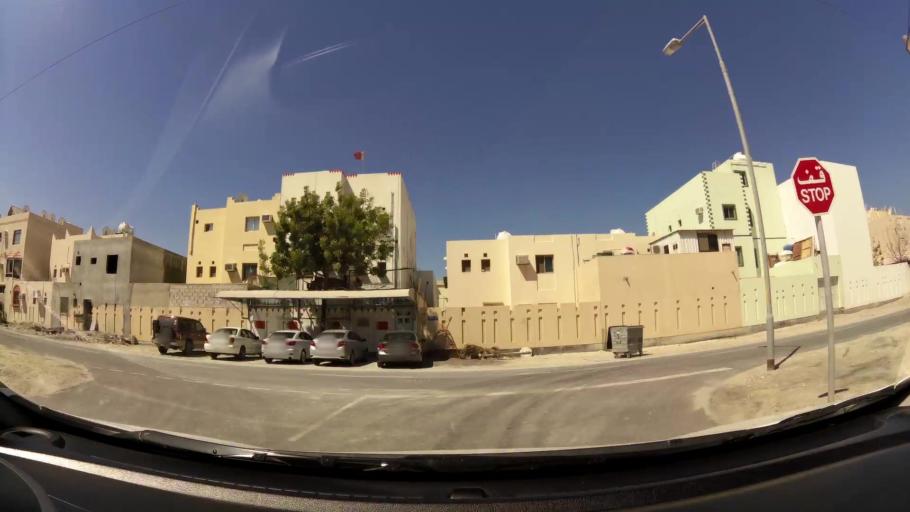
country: BH
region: Muharraq
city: Al Muharraq
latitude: 26.2710
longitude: 50.6002
